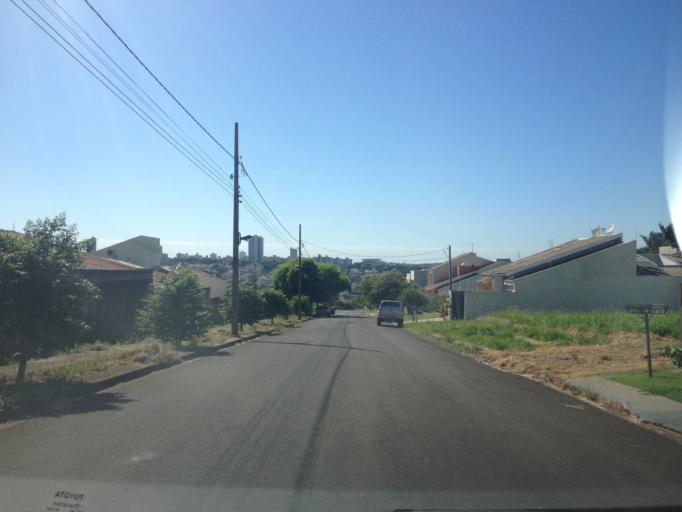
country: BR
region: Parana
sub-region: Maringa
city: Maringa
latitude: -23.4471
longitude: -51.9465
